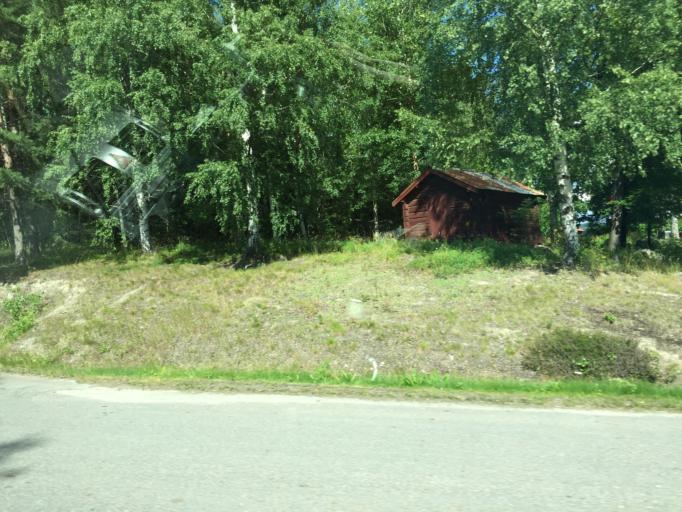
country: SE
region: Gaevleborg
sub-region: Bollnas Kommun
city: Bollnas
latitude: 61.3261
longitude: 16.4160
